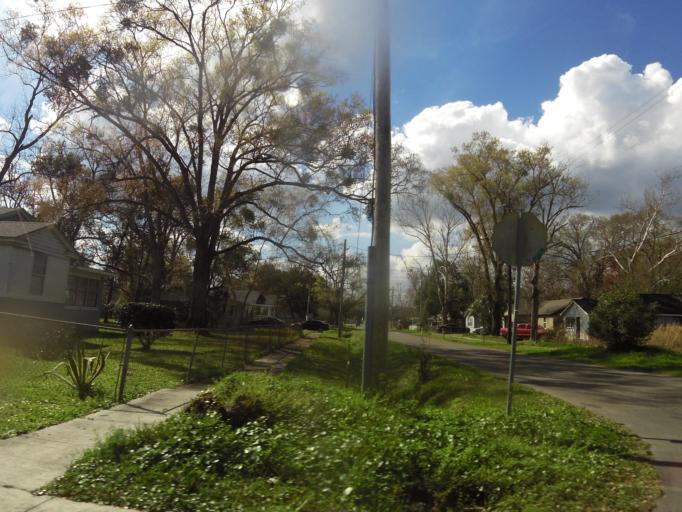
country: US
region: Florida
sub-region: Duval County
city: Jacksonville
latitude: 30.3348
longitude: -81.7141
